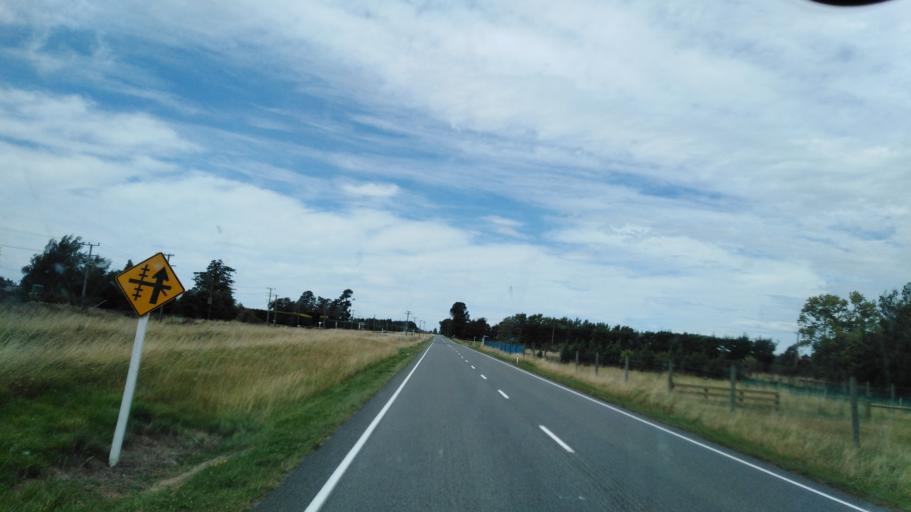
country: NZ
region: Canterbury
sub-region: Selwyn District
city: Darfield
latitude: -43.3716
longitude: 171.9893
